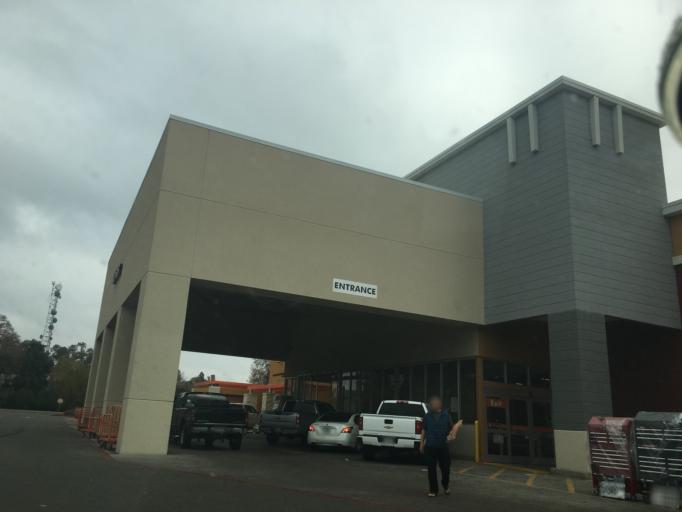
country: US
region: California
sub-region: Yolo County
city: West Sacramento
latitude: 38.5907
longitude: -121.5470
